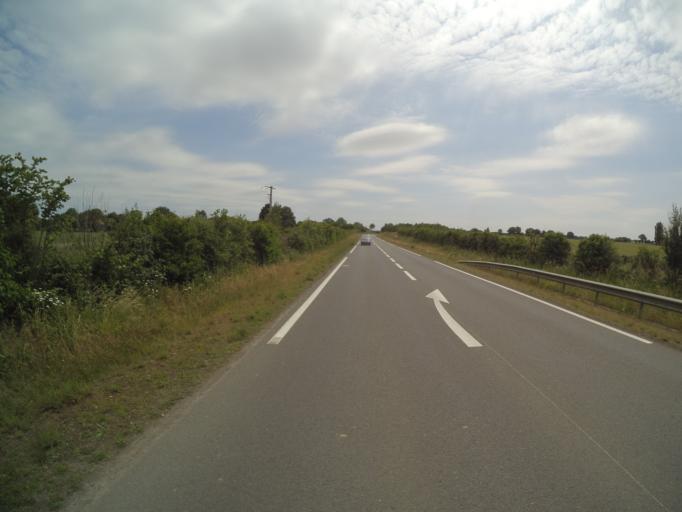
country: FR
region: Pays de la Loire
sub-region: Departement de la Vendee
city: Les Herbiers
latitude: 46.8459
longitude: -1.0184
